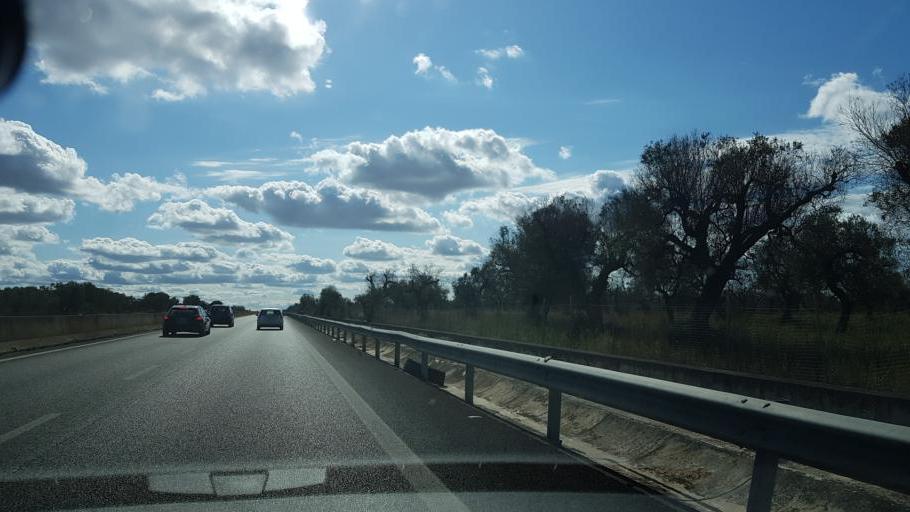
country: IT
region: Apulia
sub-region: Provincia di Lecce
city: Squinzano
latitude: 40.4507
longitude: 18.0678
